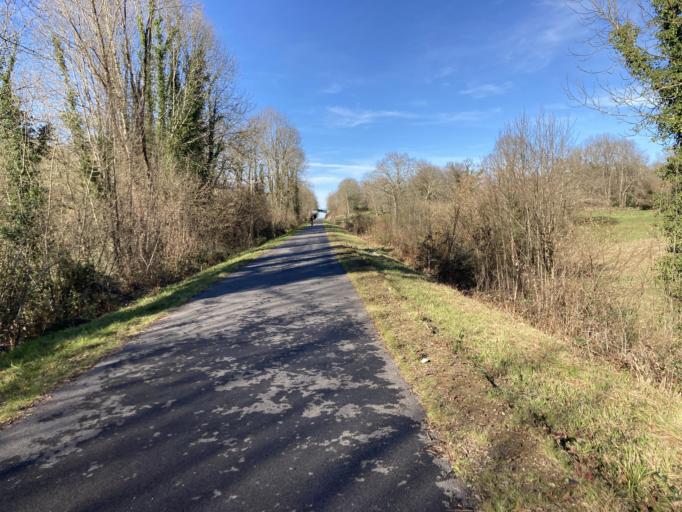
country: FR
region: Aquitaine
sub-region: Departement des Pyrenees-Atlantiques
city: Arudy
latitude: 43.1231
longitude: -0.4399
